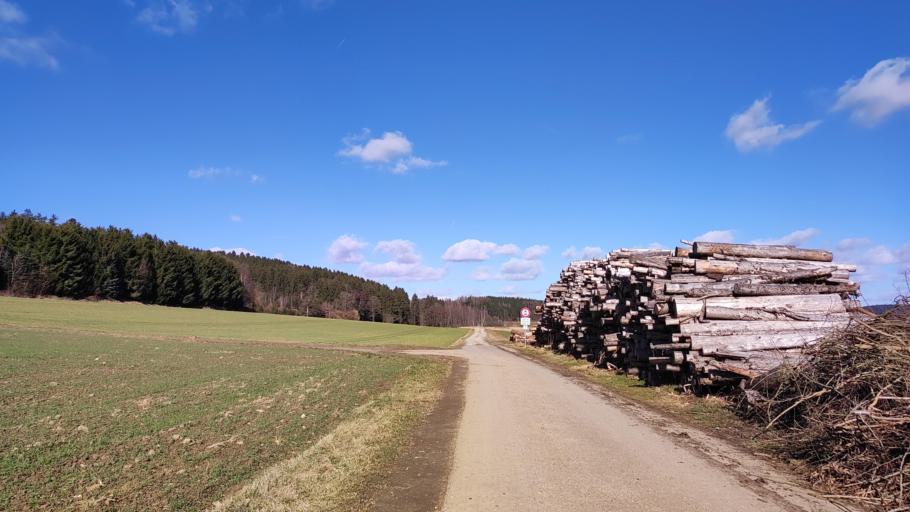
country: DE
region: Bavaria
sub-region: Swabia
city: Zusmarshausen
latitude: 48.4240
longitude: 10.5907
